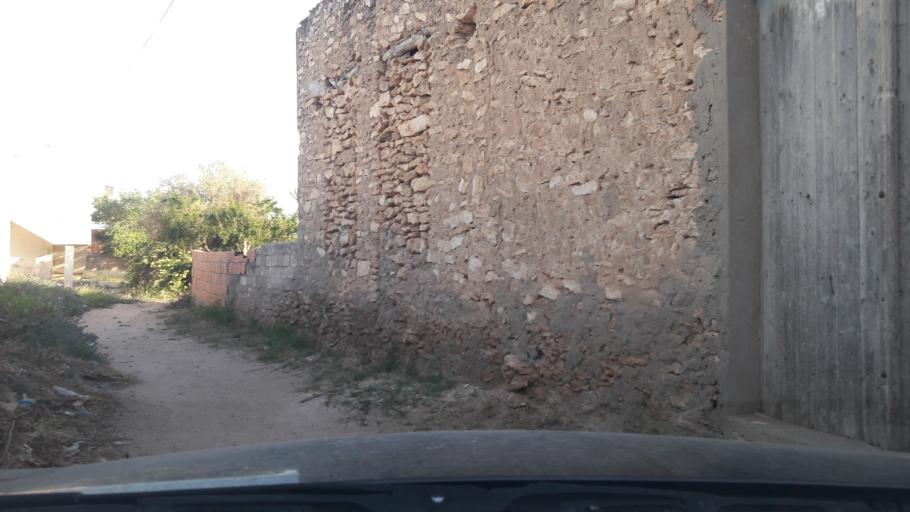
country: TN
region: Safaqis
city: Al Qarmadah
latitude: 34.7944
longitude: 10.7580
